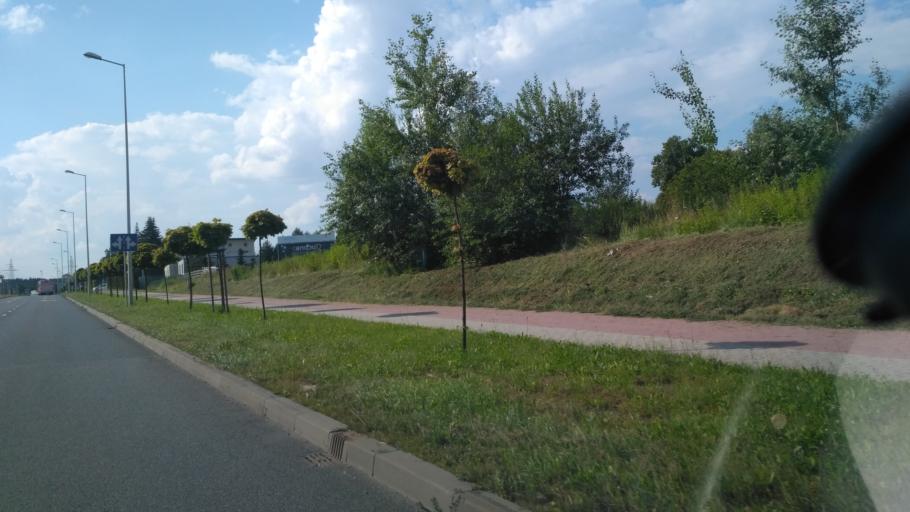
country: PL
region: Subcarpathian Voivodeship
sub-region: Powiat rzeszowski
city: Boguchwala
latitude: 50.0112
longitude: 21.9639
